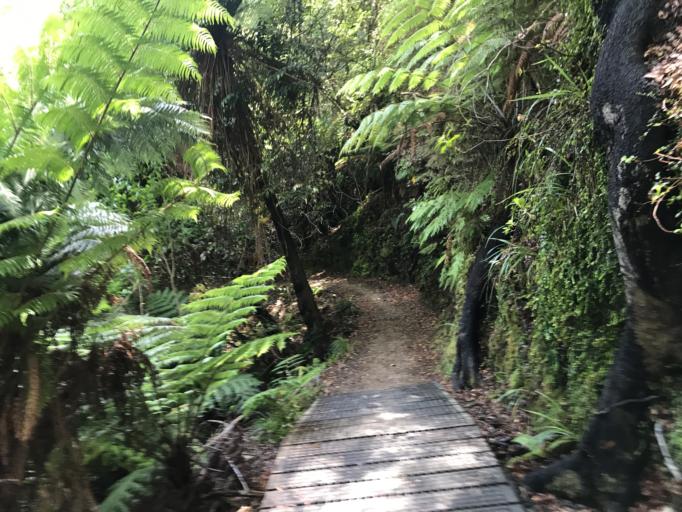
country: NZ
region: Marlborough
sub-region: Marlborough District
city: Picton
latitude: -41.2475
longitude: 173.9551
